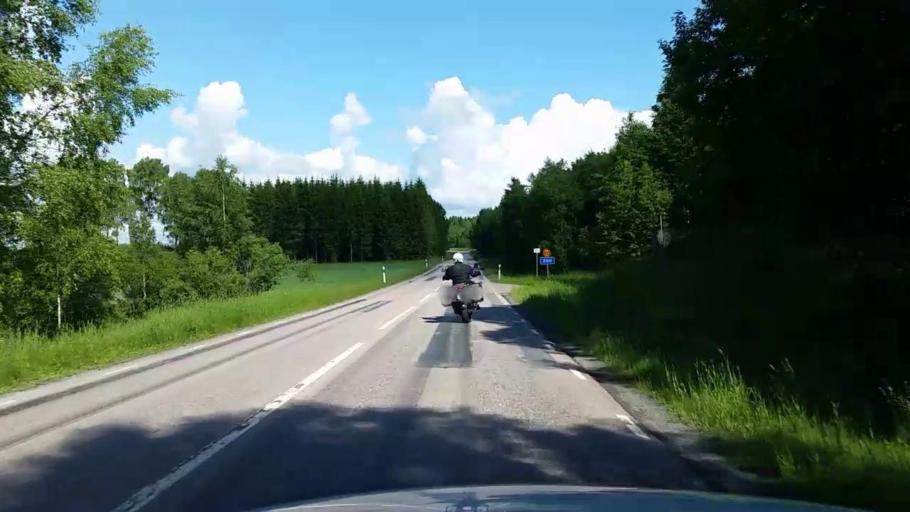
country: SE
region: Vaestmanland
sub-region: Kopings Kommun
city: Kolsva
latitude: 59.6096
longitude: 15.8285
